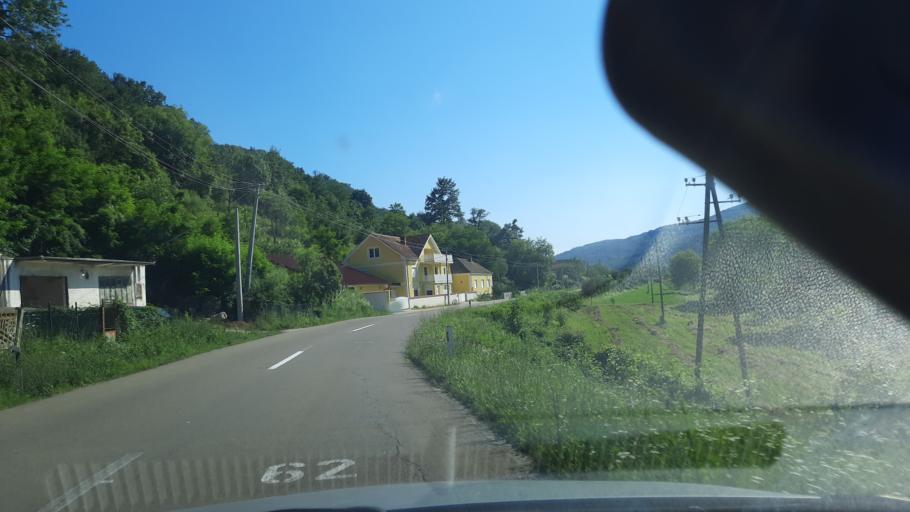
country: RS
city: Turija
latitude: 44.5136
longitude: 21.6381
